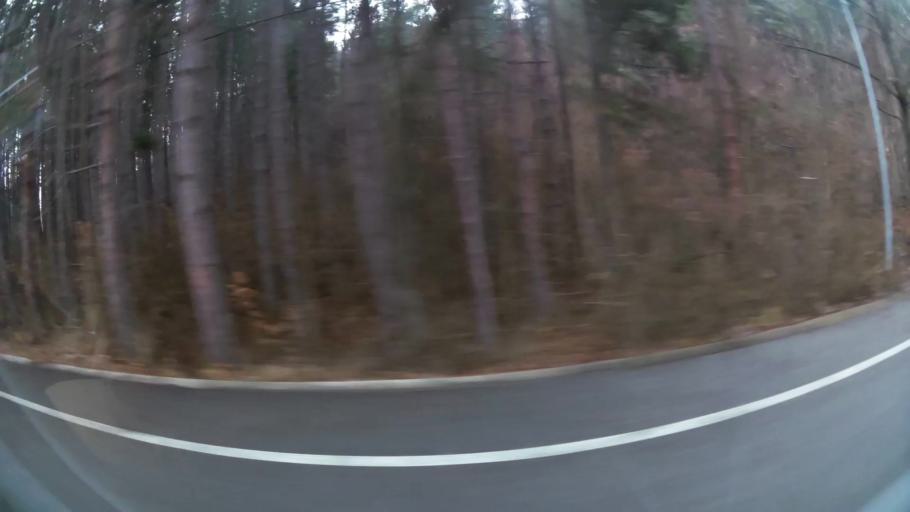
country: BG
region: Sofia-Capital
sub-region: Stolichna Obshtina
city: Sofia
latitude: 42.5856
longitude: 23.4276
